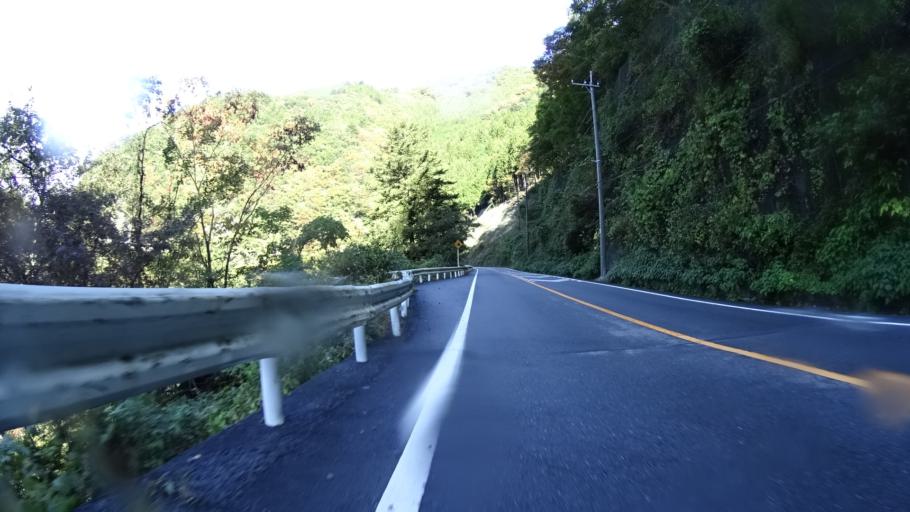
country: JP
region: Yamanashi
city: Otsuki
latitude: 35.7864
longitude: 138.9569
